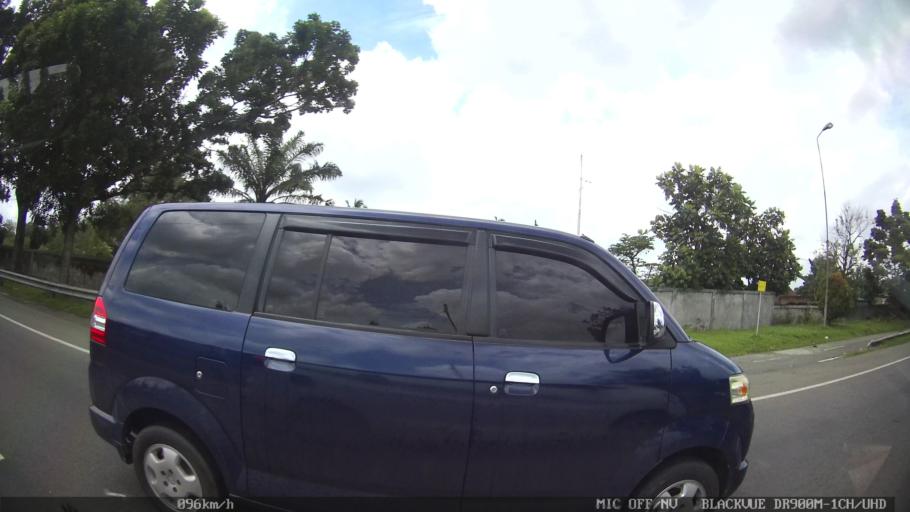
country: ID
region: North Sumatra
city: Medan
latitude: 3.6188
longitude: 98.7205
